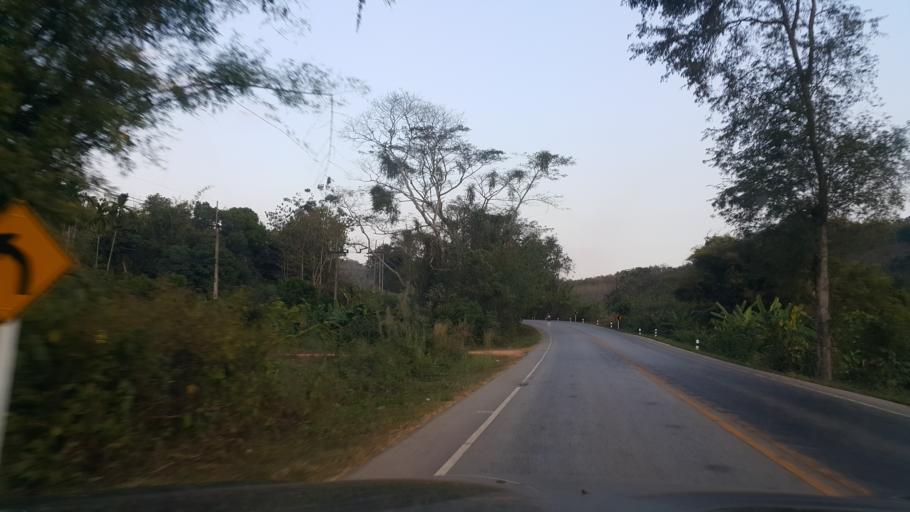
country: TH
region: Loei
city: Loei
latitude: 17.4673
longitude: 101.5883
